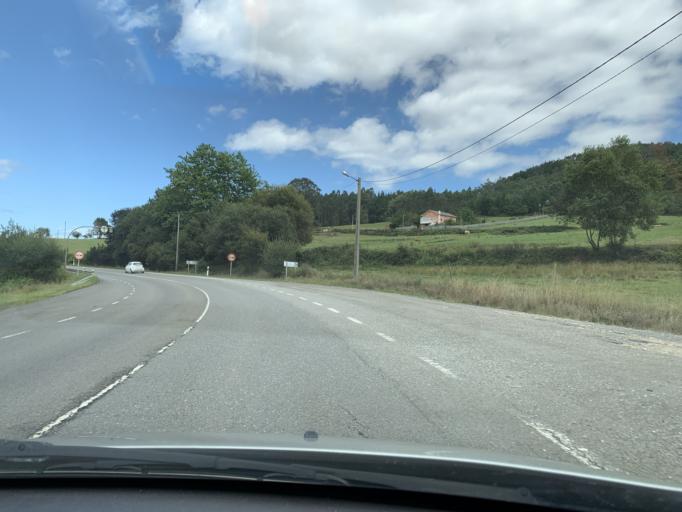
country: ES
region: Galicia
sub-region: Provincia de Lugo
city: Barreiros
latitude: 43.5215
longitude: -7.2686
